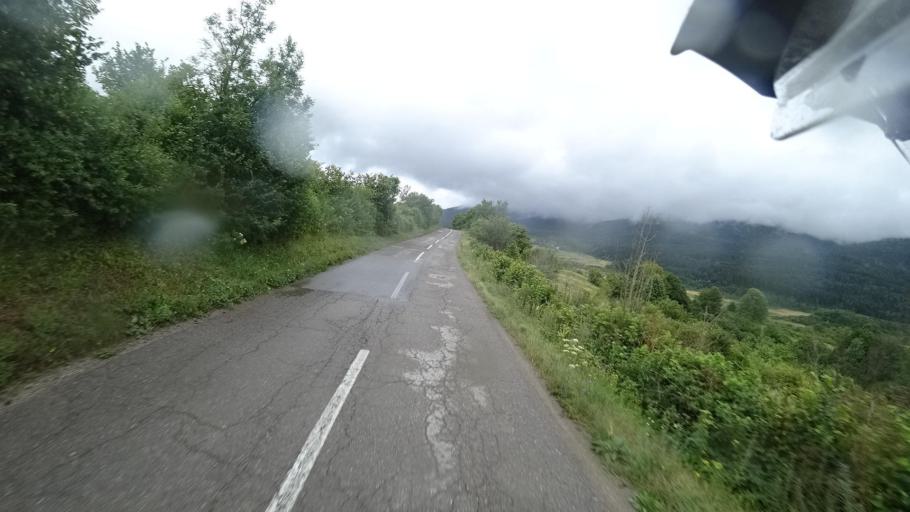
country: HR
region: Karlovacka
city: Plaski
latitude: 45.0213
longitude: 15.4129
